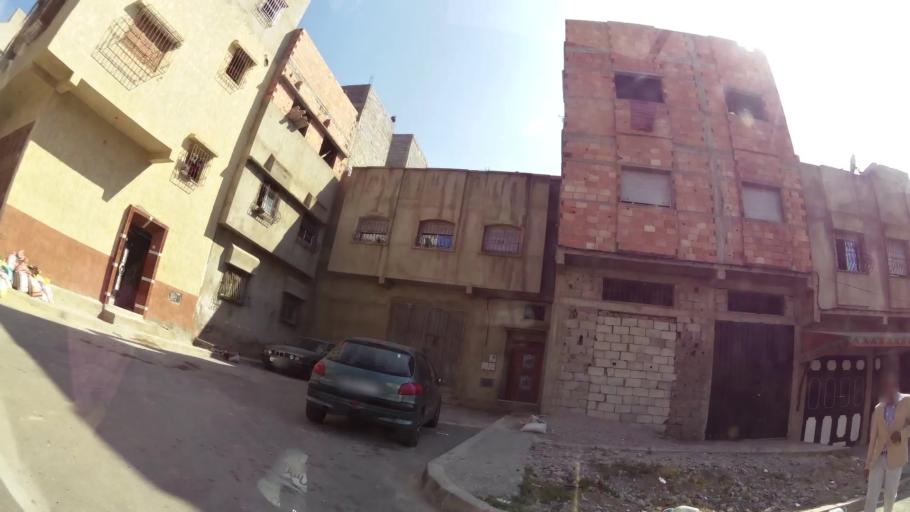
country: MA
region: Rabat-Sale-Zemmour-Zaer
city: Sale
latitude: 34.0691
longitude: -6.7713
